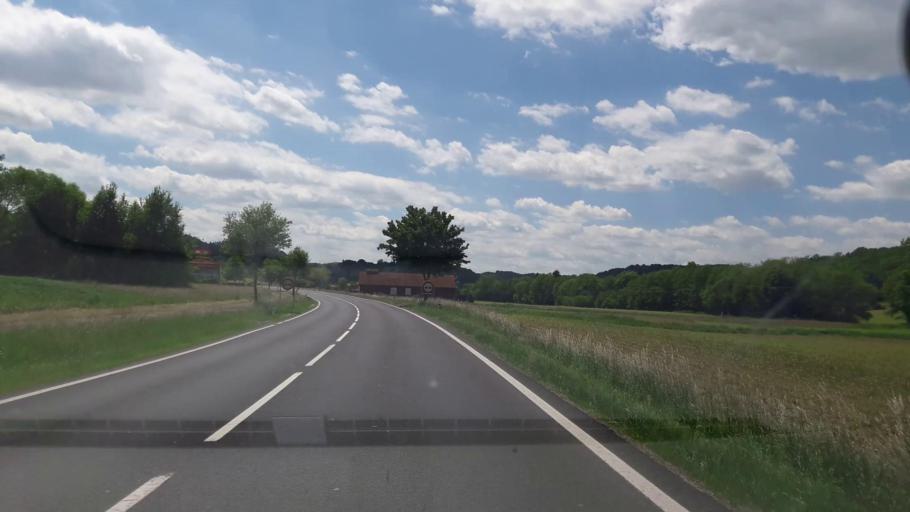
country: AT
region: Burgenland
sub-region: Politischer Bezirk Jennersdorf
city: Muhlgraben
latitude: 46.8867
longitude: 16.0830
